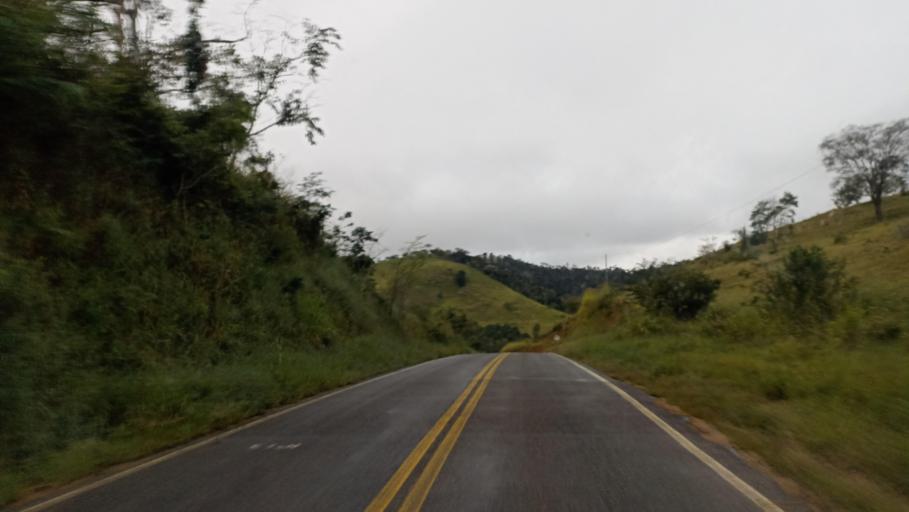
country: BR
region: Bahia
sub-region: Itanhem
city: Itanhem
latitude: -16.6910
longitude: -40.5131
